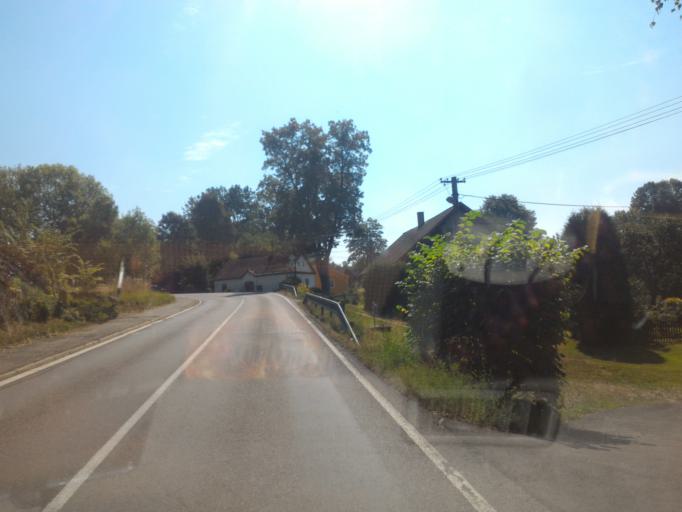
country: CZ
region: Pardubicky
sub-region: Okres Chrudim
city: Hlinsko
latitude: 49.7701
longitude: 15.8521
